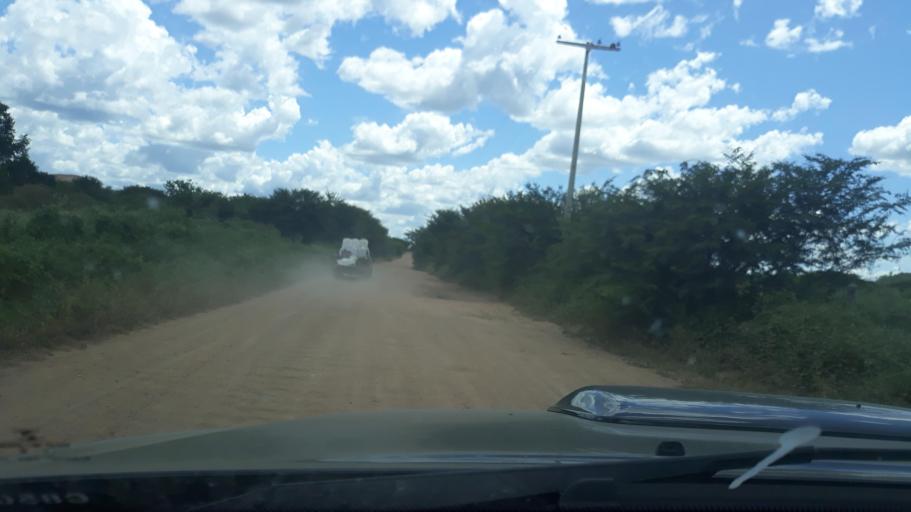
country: BR
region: Bahia
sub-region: Riacho De Santana
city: Riacho de Santana
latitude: -13.9047
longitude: -42.9237
